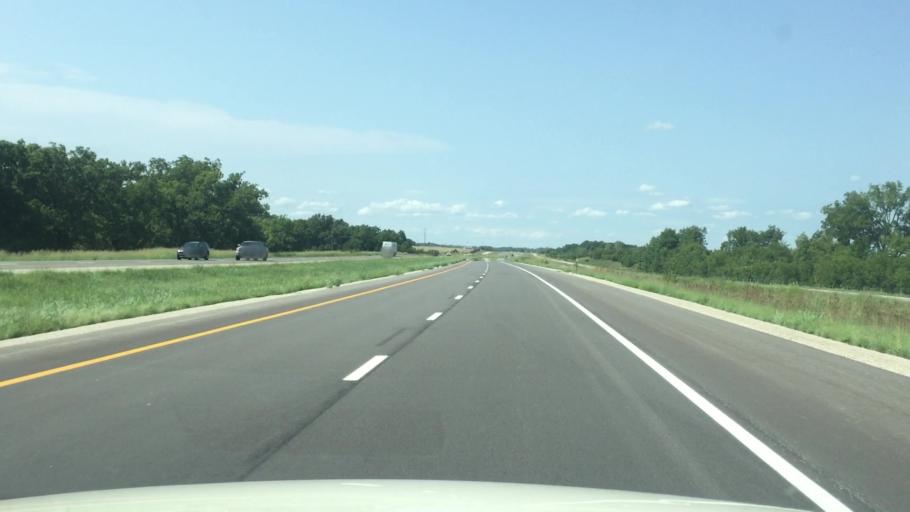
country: US
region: Kansas
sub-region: Linn County
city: La Cygne
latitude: 38.3060
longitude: -94.6773
